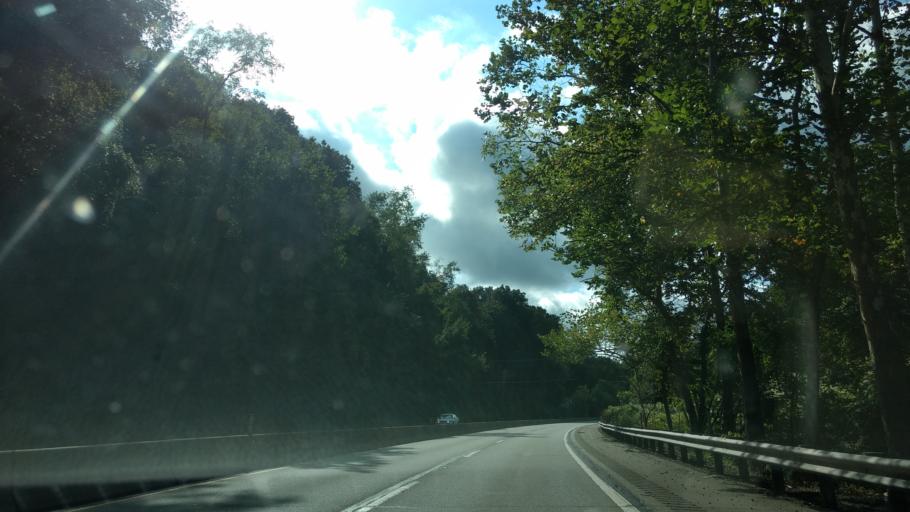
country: US
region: Pennsylvania
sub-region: Allegheny County
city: Elizabeth
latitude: 40.2457
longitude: -79.8732
